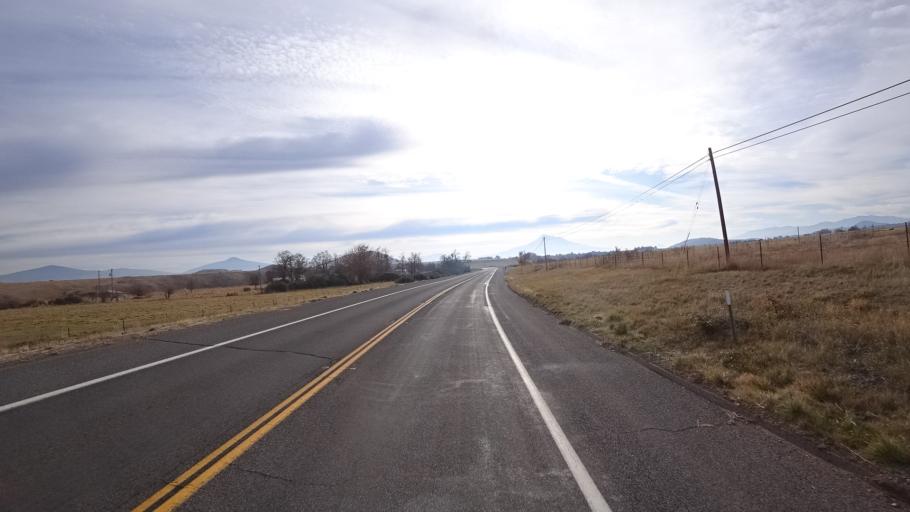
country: US
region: California
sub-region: Siskiyou County
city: Montague
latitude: 41.7280
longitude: -122.5614
